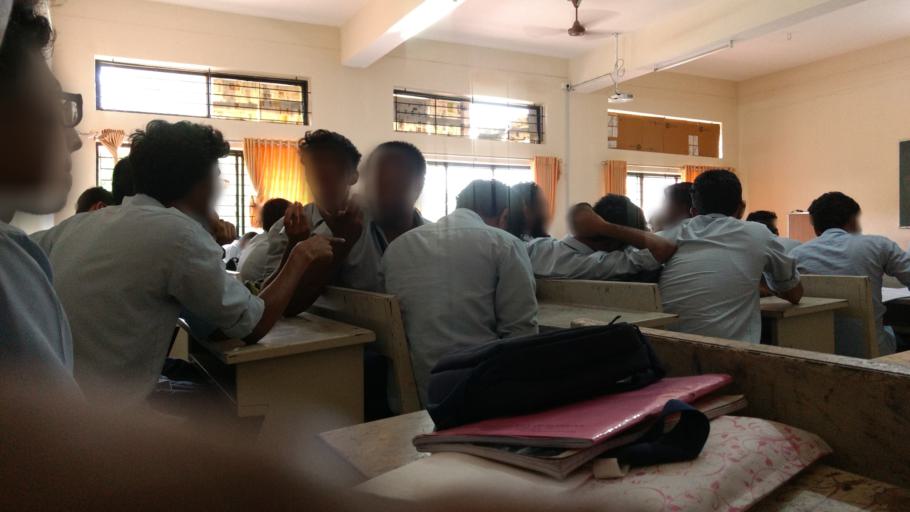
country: IN
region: Kerala
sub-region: Thrissur District
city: Avanoor
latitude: 10.6268
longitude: 76.1461
